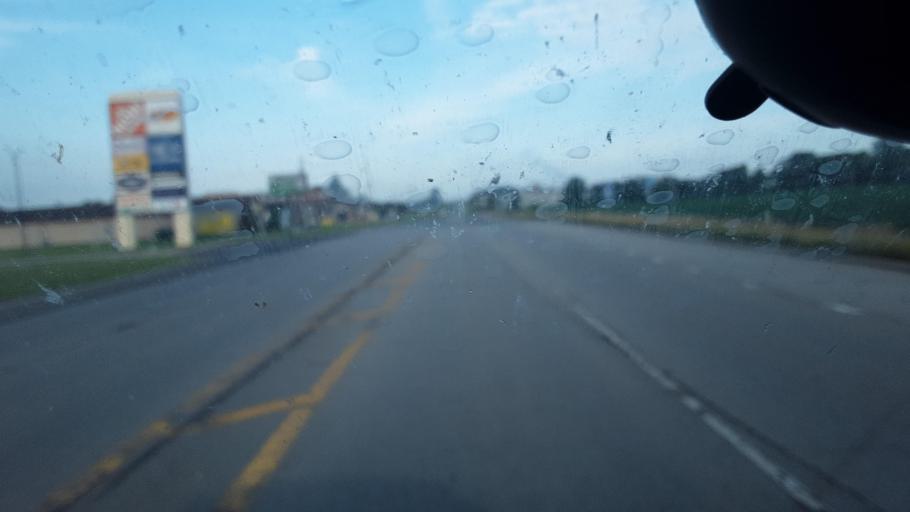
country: US
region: Indiana
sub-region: DeKalb County
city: Auburn
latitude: 41.3668
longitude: -85.0849
